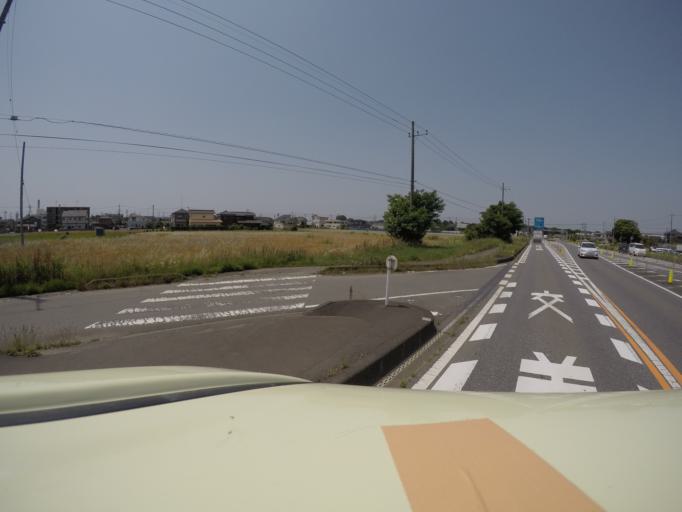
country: JP
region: Ibaraki
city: Mitsukaido
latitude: 36.0360
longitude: 139.9901
